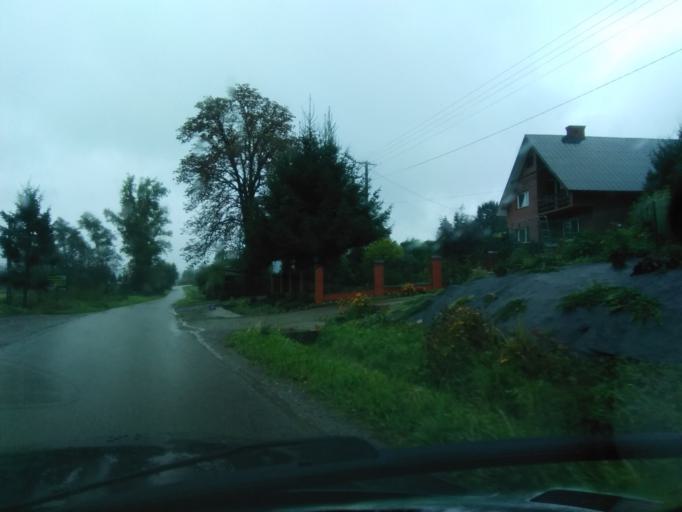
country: PL
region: Subcarpathian Voivodeship
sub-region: Powiat ropczycko-sedziszowski
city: Niedzwiada
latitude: 50.0076
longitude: 21.5498
